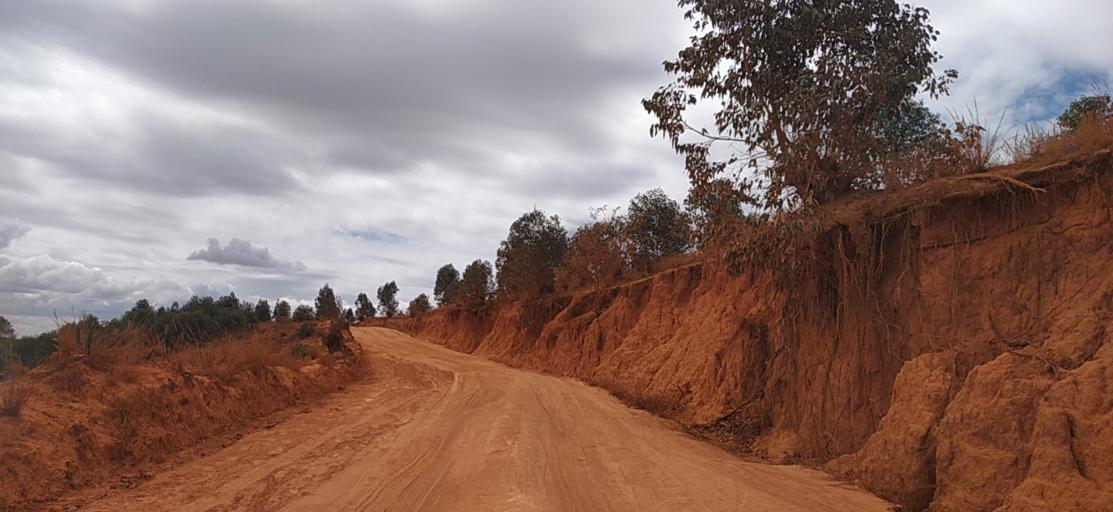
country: MG
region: Alaotra Mangoro
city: Ambatondrazaka
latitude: -18.0486
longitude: 48.2495
